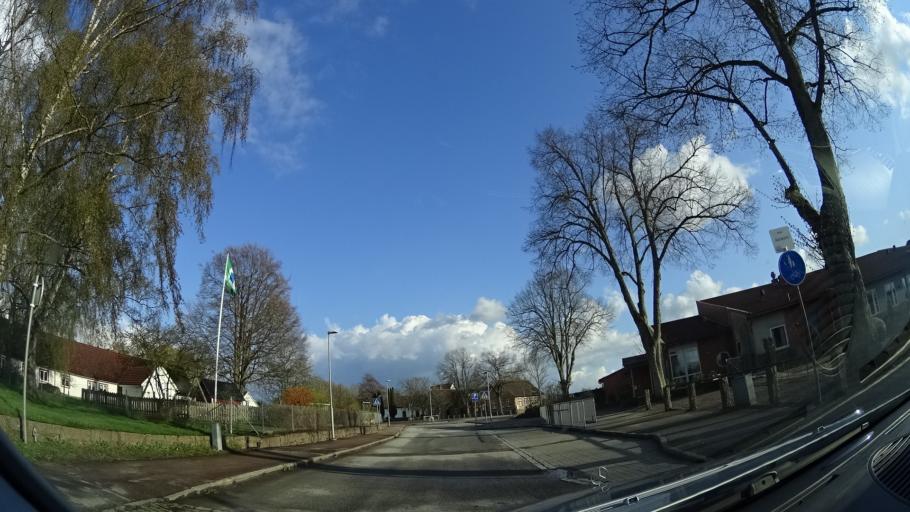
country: SE
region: Skane
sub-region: Klippans Kommun
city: Ljungbyhed
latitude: 55.9998
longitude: 13.2944
